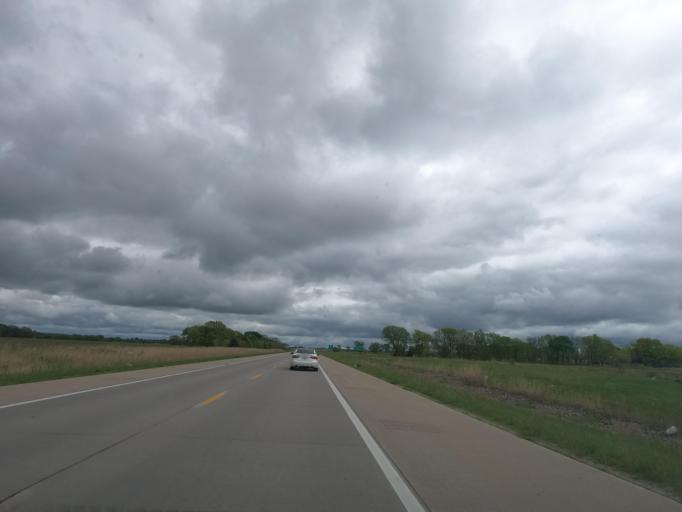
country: US
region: Kansas
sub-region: Montgomery County
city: Cherryvale
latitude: 37.3469
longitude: -95.5504
